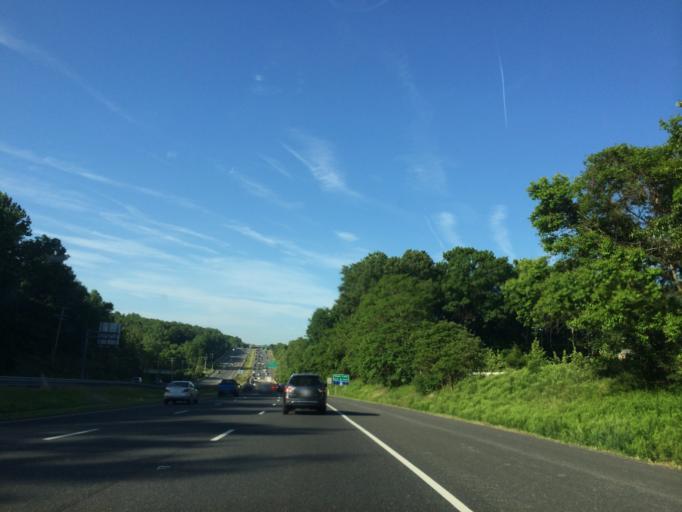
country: US
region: Maryland
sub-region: Howard County
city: Riverside
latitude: 39.1717
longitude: -76.8830
